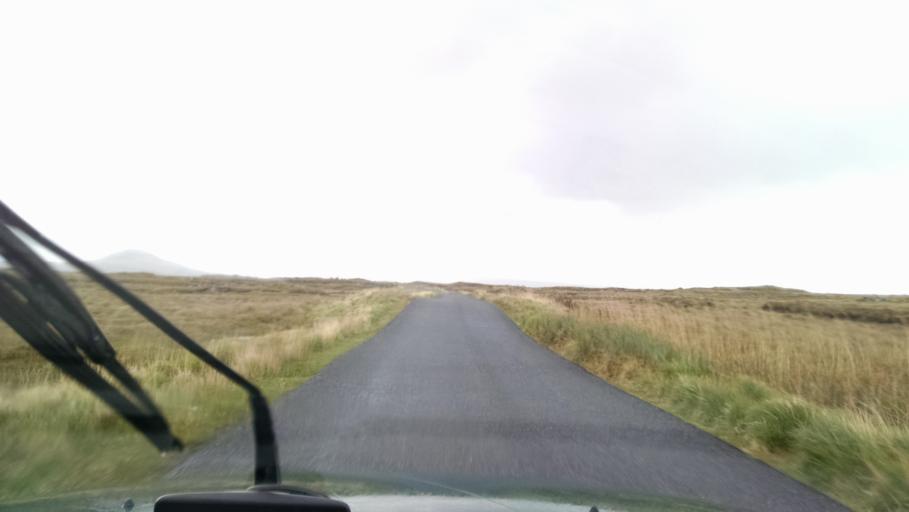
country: IE
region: Connaught
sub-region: County Galway
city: Clifden
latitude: 53.4381
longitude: -9.9170
